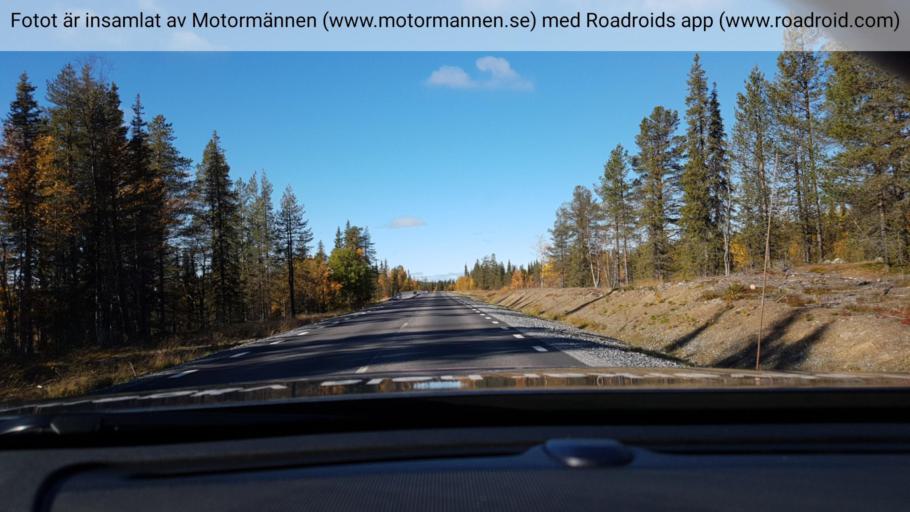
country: SE
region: Norrbotten
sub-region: Gallivare Kommun
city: Gaellivare
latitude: 66.9640
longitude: 20.7692
